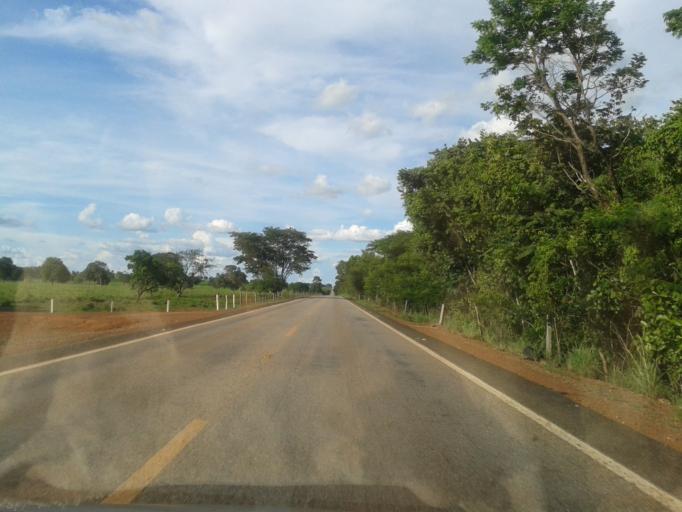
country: BR
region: Goias
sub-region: Mozarlandia
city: Mozarlandia
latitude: -14.2833
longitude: -50.4014
